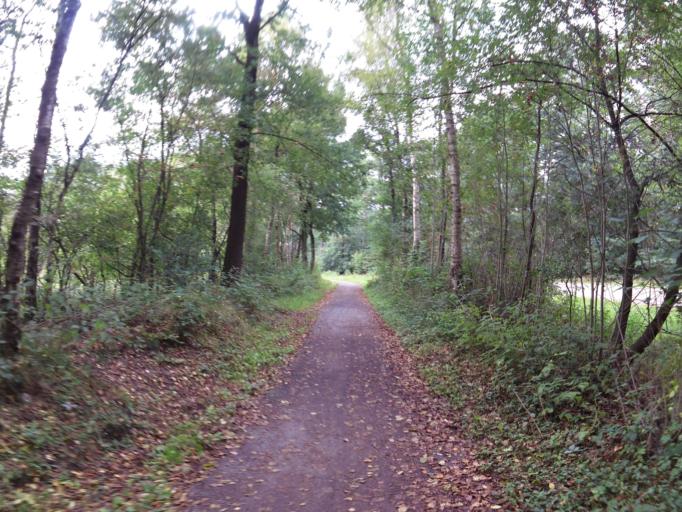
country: NL
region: Drenthe
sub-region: Gemeente Westerveld
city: Dwingeloo
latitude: 52.8173
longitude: 6.3736
